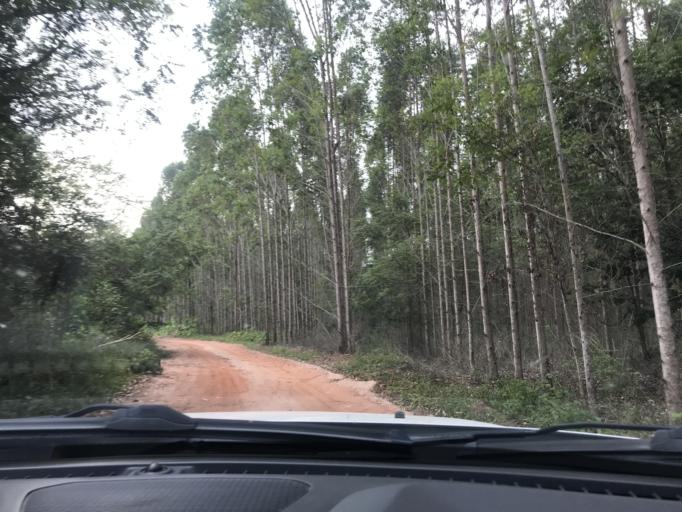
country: BR
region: Bahia
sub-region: Entre Rios
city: Entre Rios
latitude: -12.0960
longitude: -38.1916
